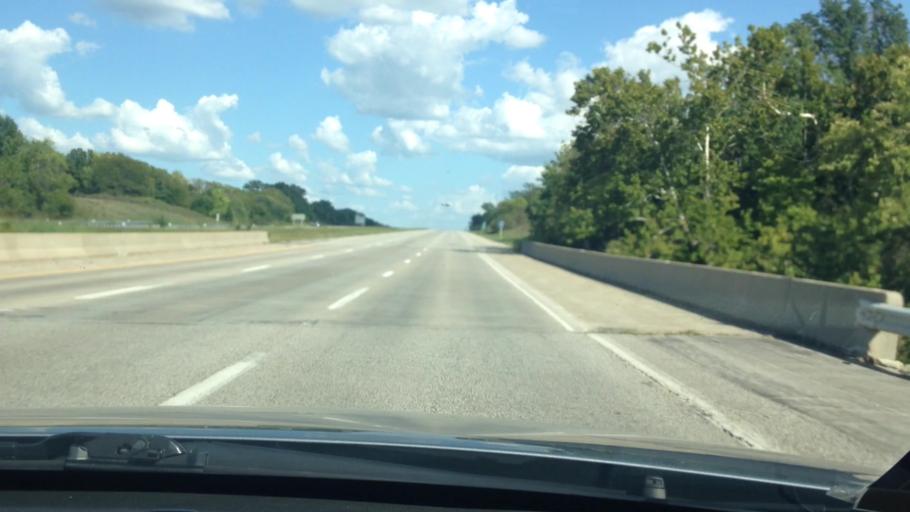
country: US
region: Missouri
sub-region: Platte County
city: Weatherby Lake
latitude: 39.3073
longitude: -94.6425
